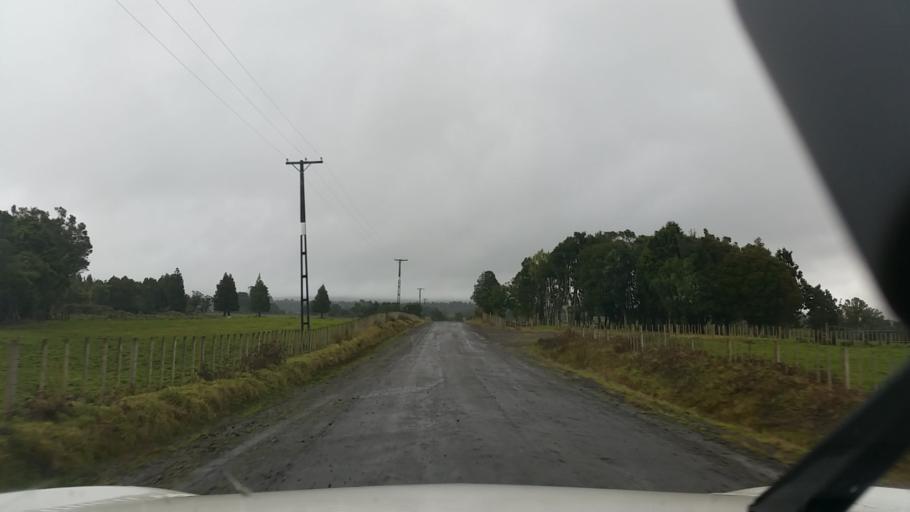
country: NZ
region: Taranaki
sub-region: South Taranaki District
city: Eltham
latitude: -39.2726
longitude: 174.1959
